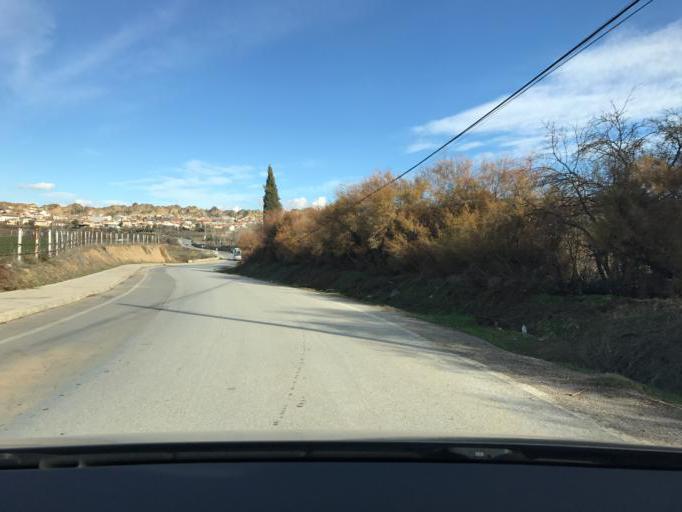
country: ES
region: Andalusia
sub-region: Provincia de Granada
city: Purullena
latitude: 37.3105
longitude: -3.1993
